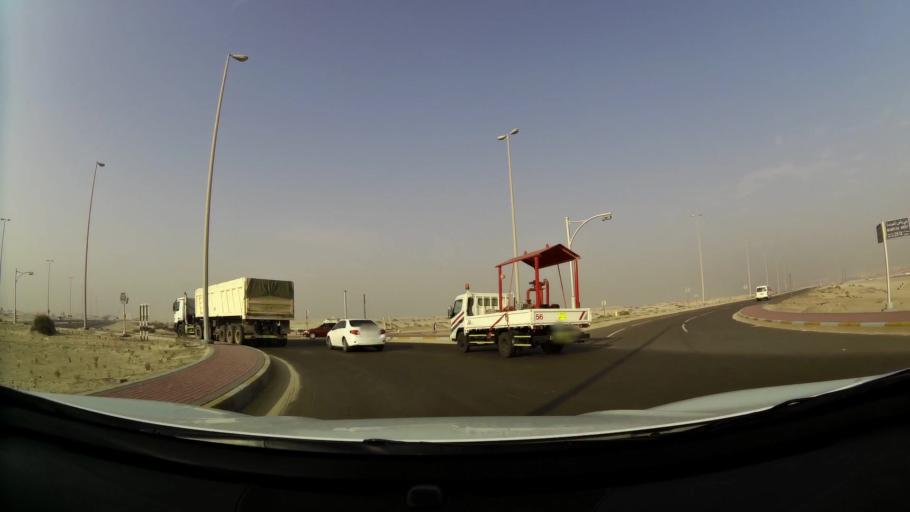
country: AE
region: Abu Dhabi
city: Abu Dhabi
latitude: 24.2757
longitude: 54.6426
